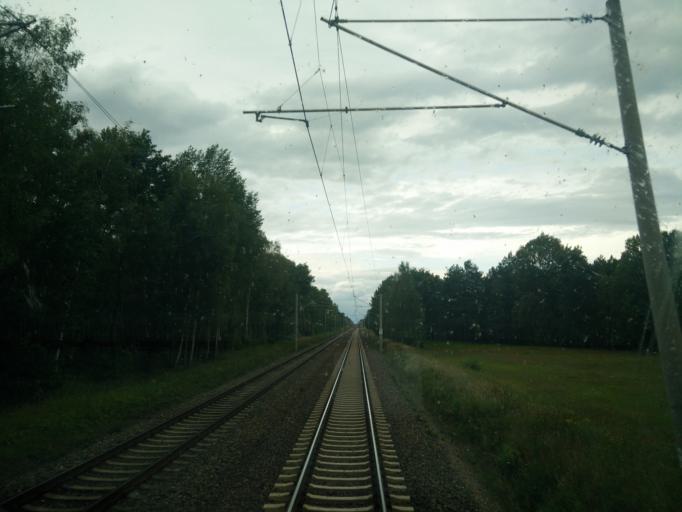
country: DE
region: Brandenburg
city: Kasel-Golzig
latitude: 51.9851
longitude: 13.7865
